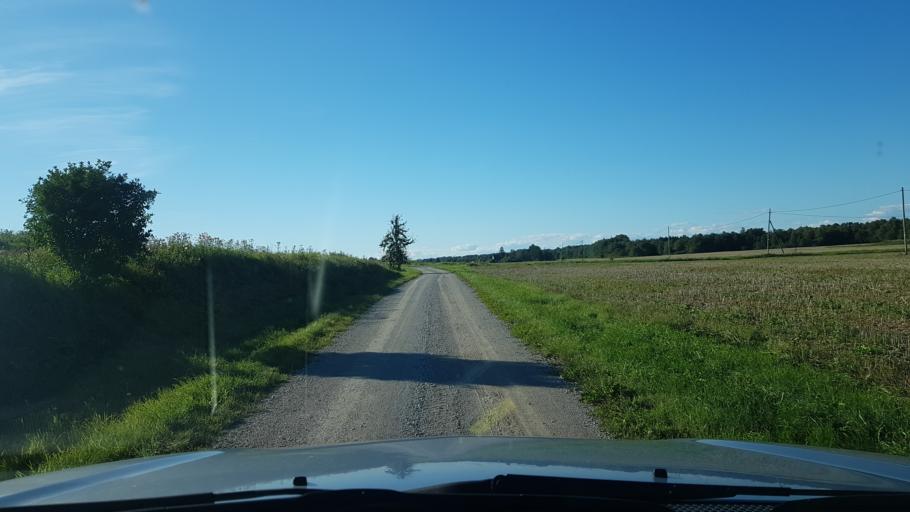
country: EE
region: Harju
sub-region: Rae vald
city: Jueri
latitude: 59.3844
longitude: 24.8816
